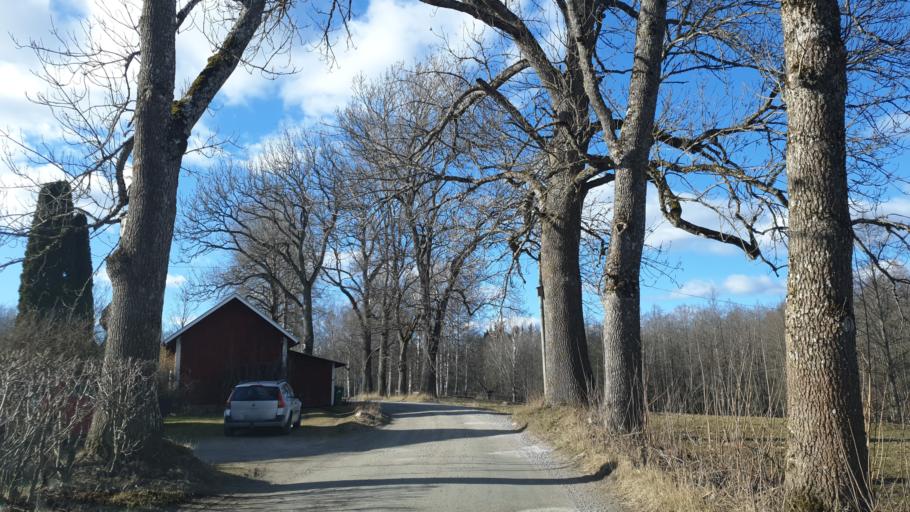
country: SE
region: OErebro
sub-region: Orebro Kommun
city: Garphyttan
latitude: 59.3457
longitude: 15.0036
